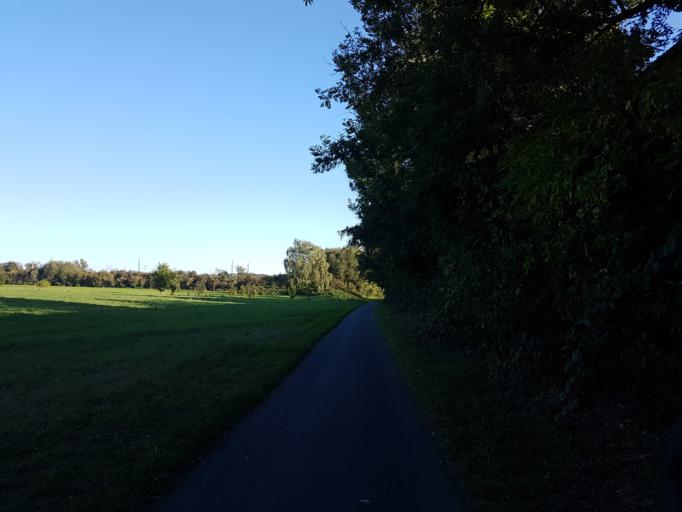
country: DE
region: North Rhine-Westphalia
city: Bad Oeynhausen
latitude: 52.2125
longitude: 8.8419
